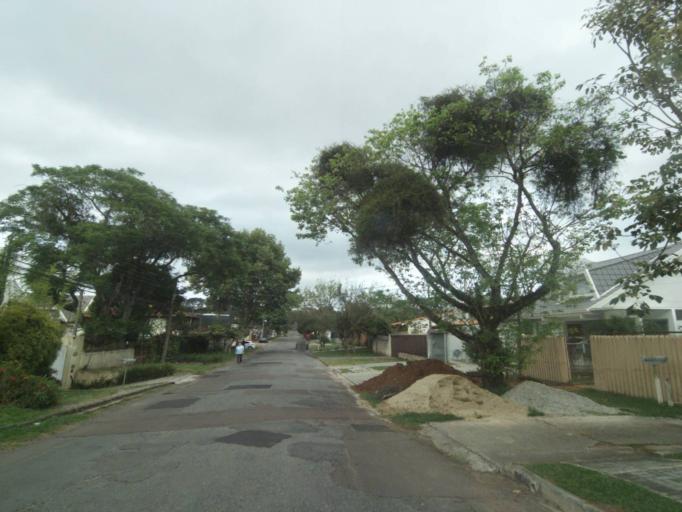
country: BR
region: Parana
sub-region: Pinhais
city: Pinhais
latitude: -25.4138
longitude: -49.2143
